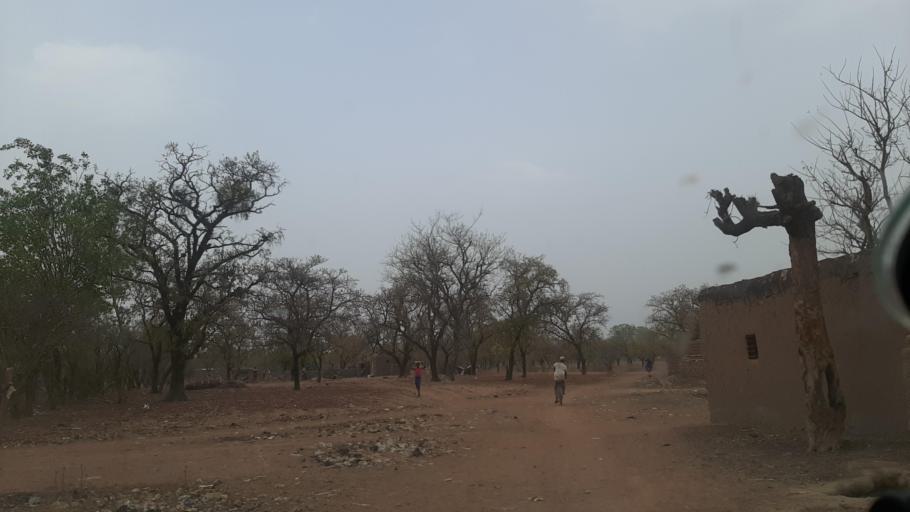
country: BF
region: Boucle du Mouhoun
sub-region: Province des Banwa
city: Salanso
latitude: 11.8692
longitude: -4.4471
